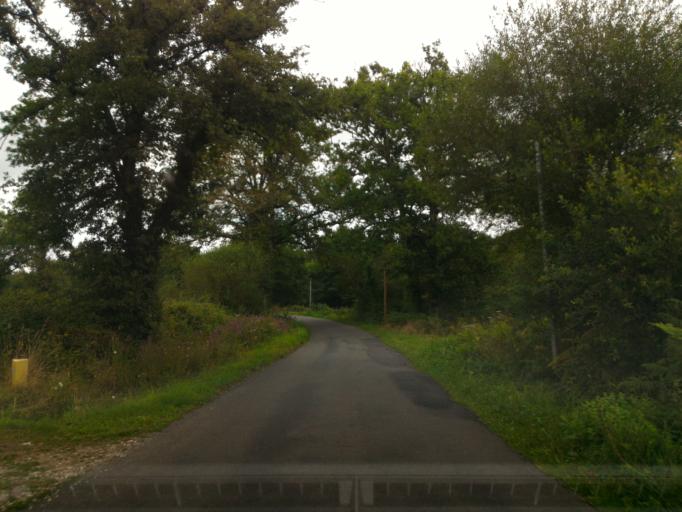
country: FR
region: Poitou-Charentes
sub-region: Departement de la Charente
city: Chabanais
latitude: 45.8845
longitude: 0.7406
